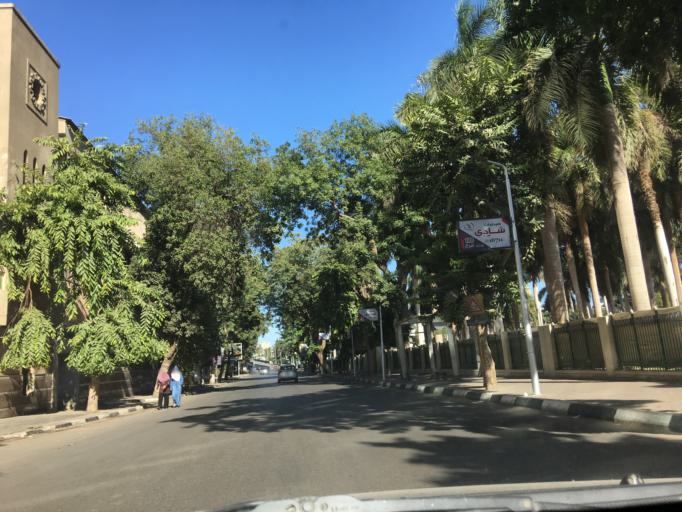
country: EG
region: Muhafazat al Qahirah
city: Cairo
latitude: 30.0447
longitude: 31.2271
